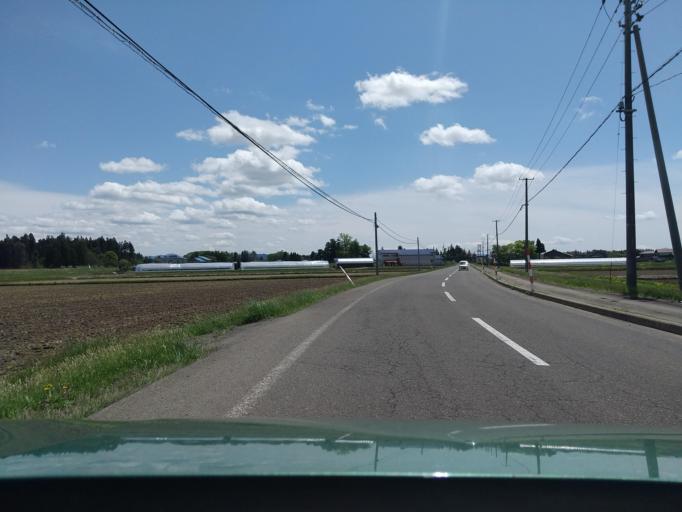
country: JP
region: Akita
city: Yokotemachi
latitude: 39.3600
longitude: 140.5382
